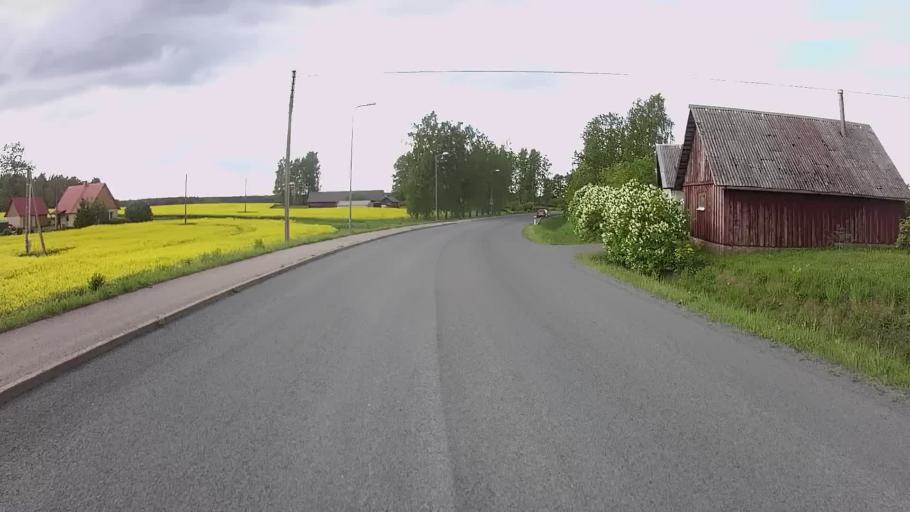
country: EE
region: Laeaene-Virumaa
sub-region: Vinni vald
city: Vinni
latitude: 59.1552
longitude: 26.5890
